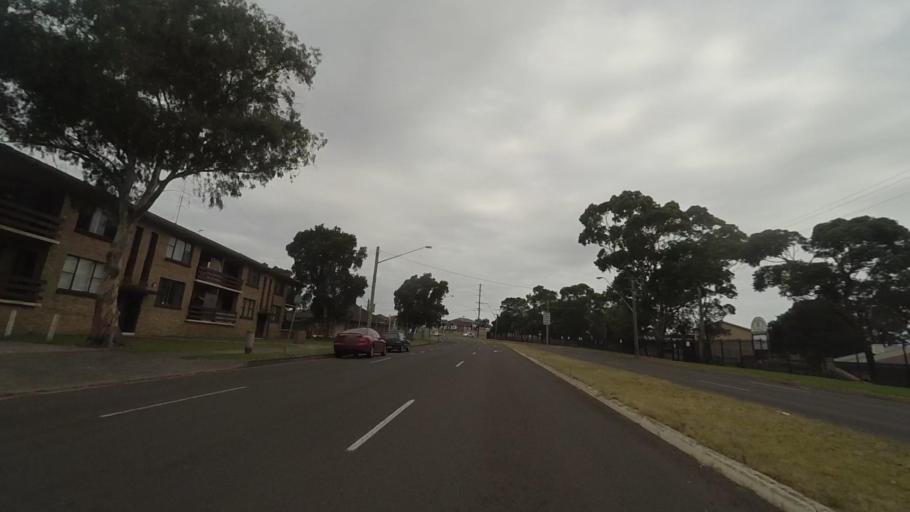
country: AU
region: New South Wales
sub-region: Wollongong
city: Port Kembla
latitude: -34.4882
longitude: 150.8928
